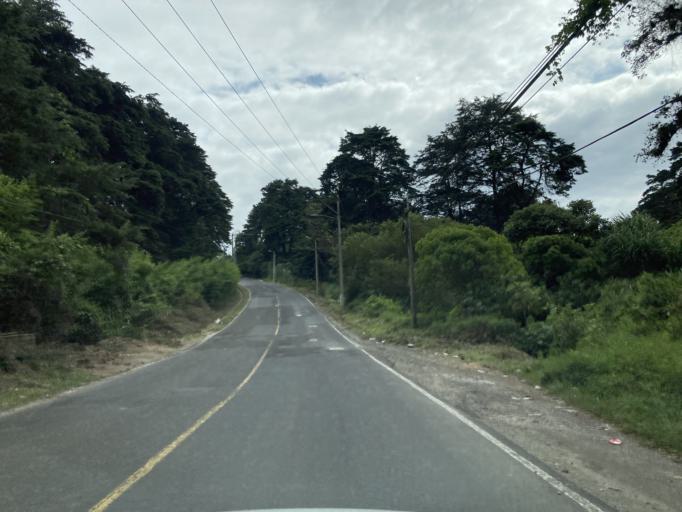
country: GT
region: Guatemala
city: San Jose Pinula
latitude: 14.5282
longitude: -90.4109
